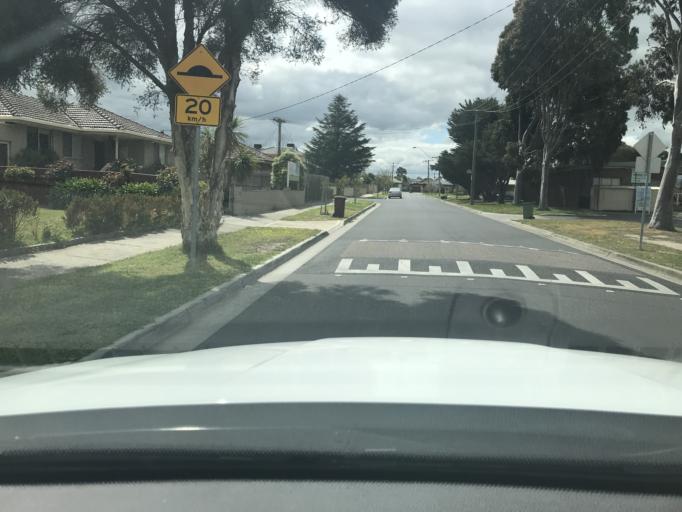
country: AU
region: Victoria
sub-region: Hume
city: Craigieburn
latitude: -37.5974
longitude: 144.9315
